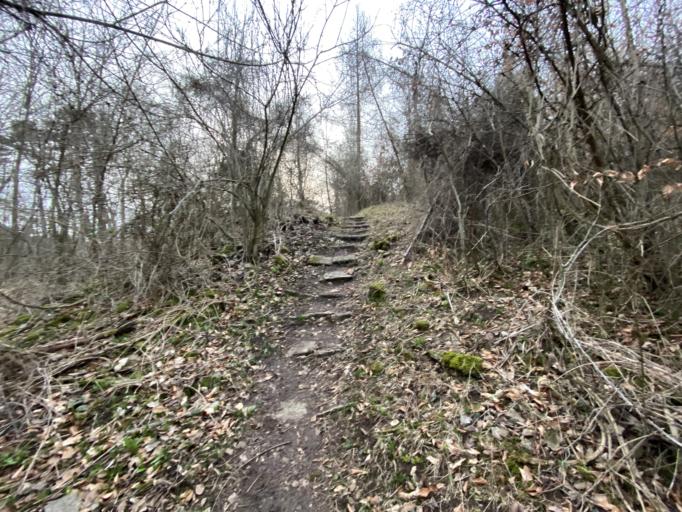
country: AT
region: Lower Austria
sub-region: Politischer Bezirk Modling
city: Gaaden
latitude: 48.0204
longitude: 16.1882
